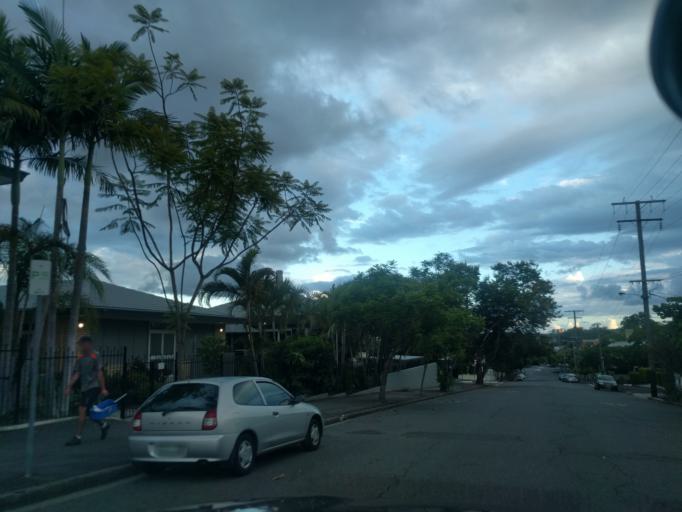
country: AU
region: Queensland
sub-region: Brisbane
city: Fortitude Valley
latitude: -27.4668
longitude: 153.0436
